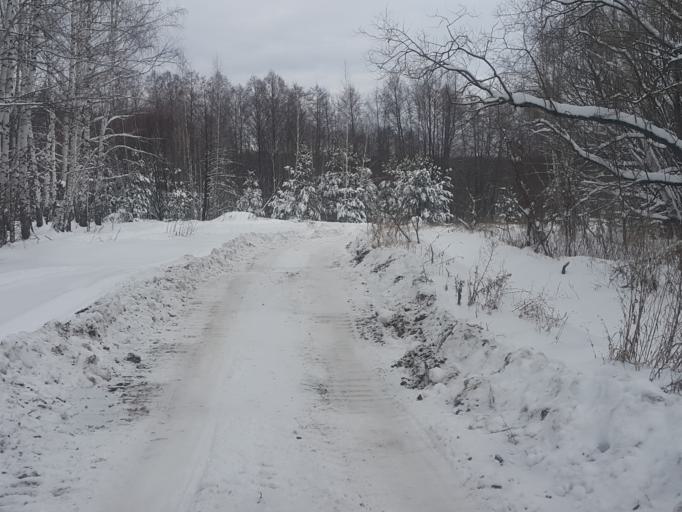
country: RU
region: Tambov
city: Platonovka
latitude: 52.8922
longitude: 41.8463
